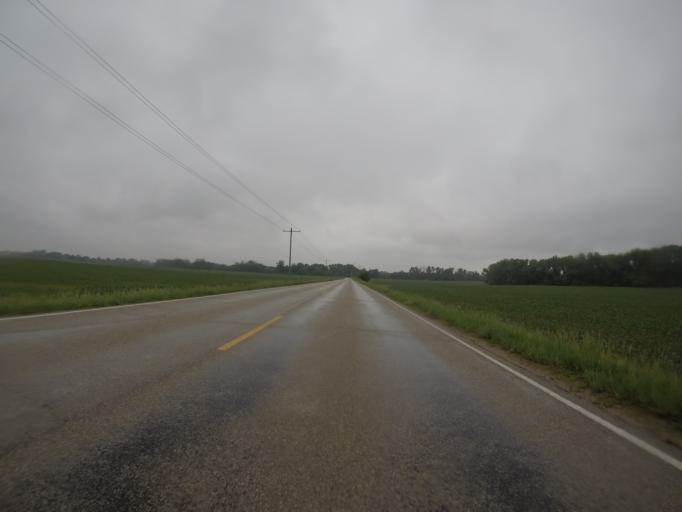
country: US
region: Kansas
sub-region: Pottawatomie County
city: Wamego
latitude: 39.2178
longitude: -96.2313
